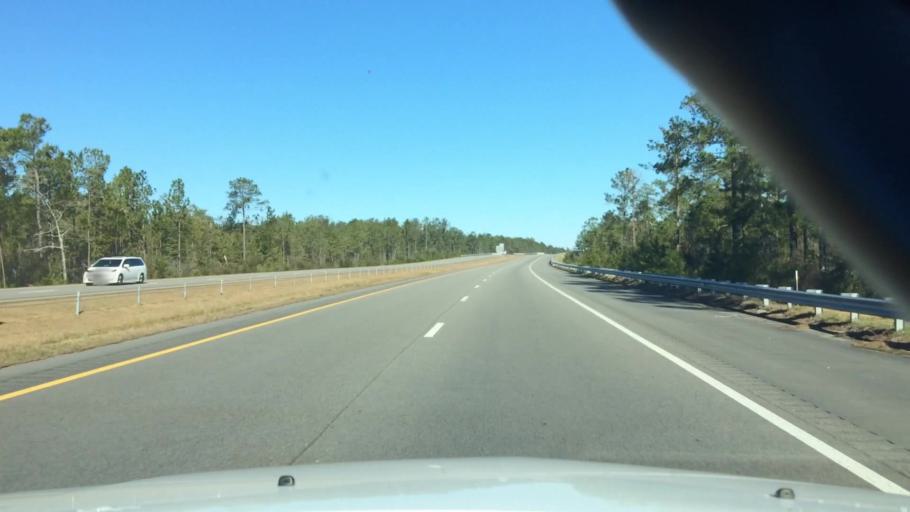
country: US
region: North Carolina
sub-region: Brunswick County
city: Leland
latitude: 34.2146
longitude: -78.0766
